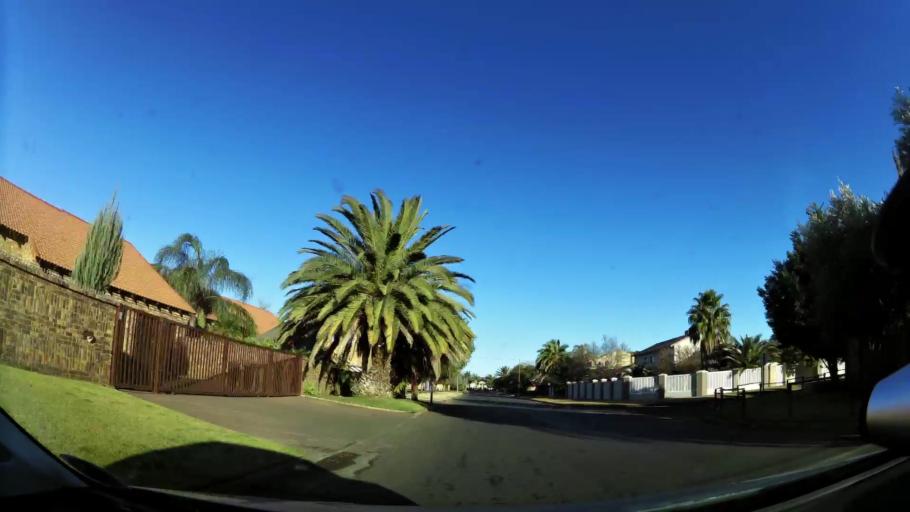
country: ZA
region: Northern Cape
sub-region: Frances Baard District Municipality
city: Kimberley
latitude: -28.7595
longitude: 24.7563
